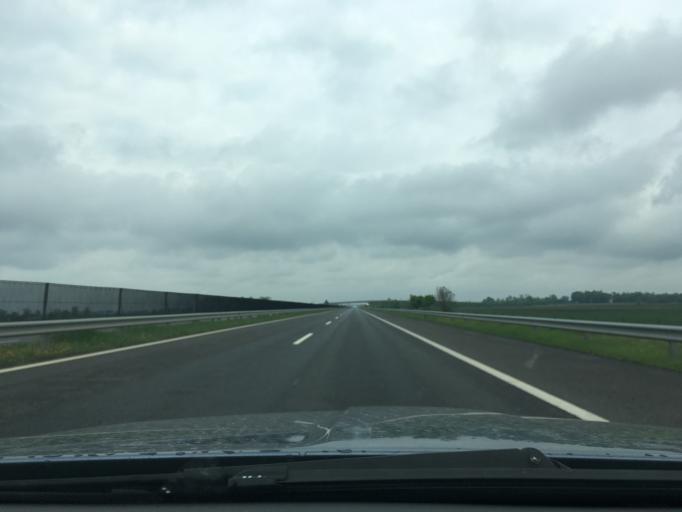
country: HU
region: Hajdu-Bihar
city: Hajduboszormeny
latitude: 47.6732
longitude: 21.4621
